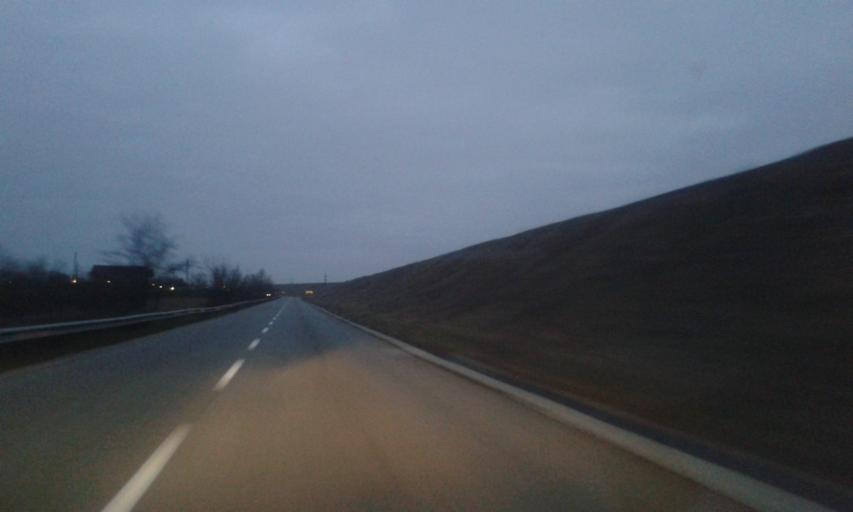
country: RO
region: Gorj
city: Targu Jiu
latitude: 45.0646
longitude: 23.2761
